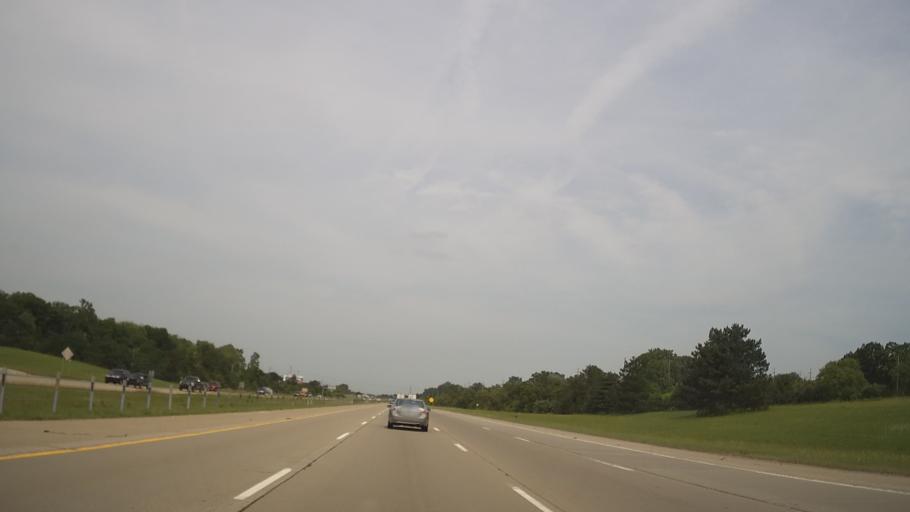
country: US
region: Michigan
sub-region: Wayne County
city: Belleville
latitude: 42.2198
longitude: -83.4845
